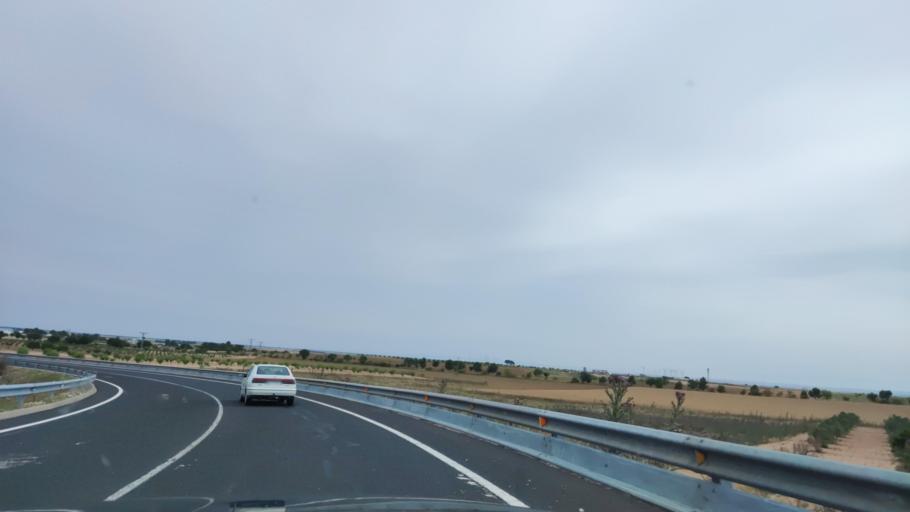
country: ES
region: Castille-La Mancha
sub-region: Provincia de Albacete
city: La Roda
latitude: 39.2199
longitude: -2.1920
